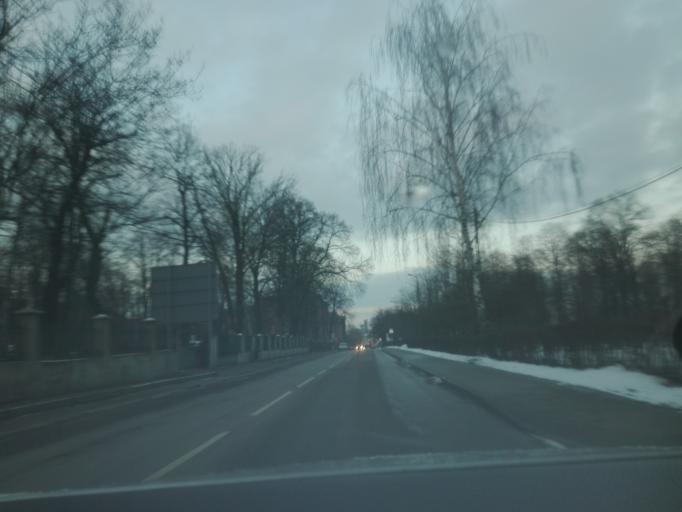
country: PL
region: Silesian Voivodeship
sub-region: Katowice
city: Katowice
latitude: 50.2522
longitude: 19.0299
